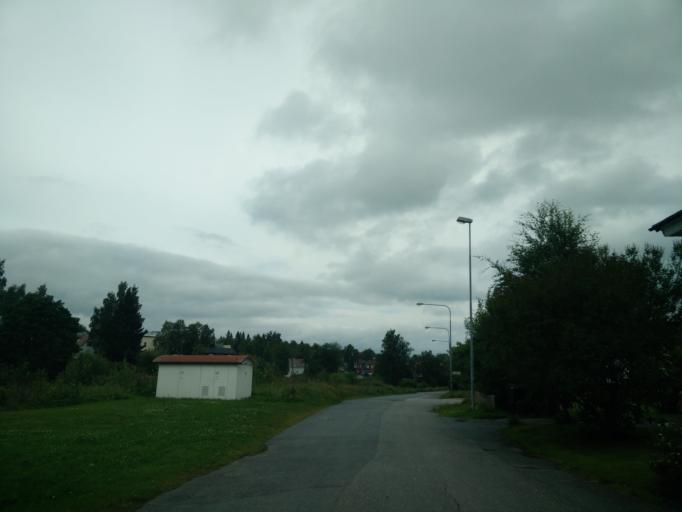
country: SE
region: Vaesternorrland
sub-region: Haernoesands Kommun
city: Haernoesand
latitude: 62.6293
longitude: 17.9179
